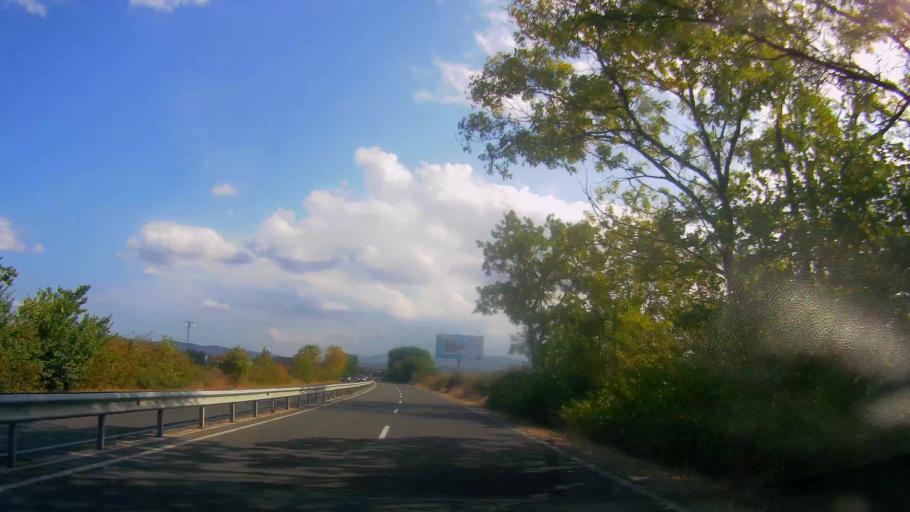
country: BG
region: Burgas
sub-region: Obshtina Sozopol
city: Chernomorets
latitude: 42.4341
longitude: 27.6376
